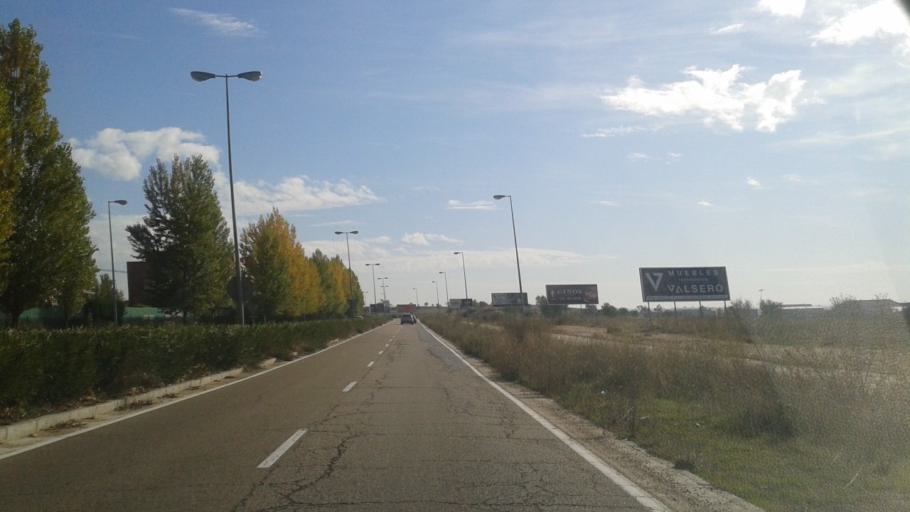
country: ES
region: Castille and Leon
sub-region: Provincia de Valladolid
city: Zaratan
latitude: 41.6336
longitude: -4.7734
